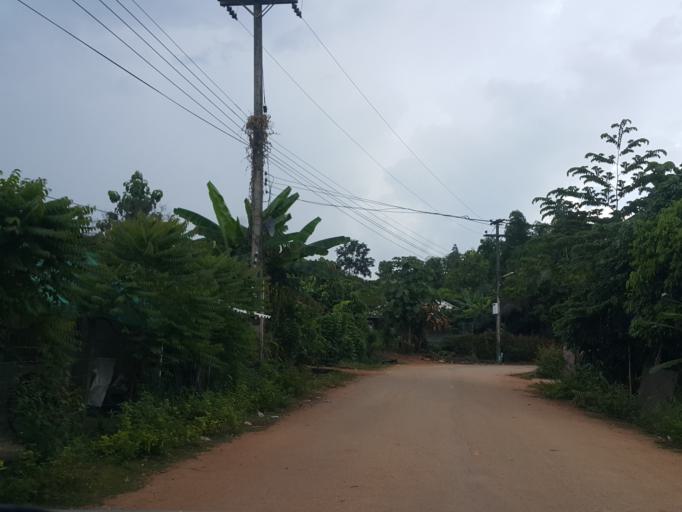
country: TH
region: Chiang Mai
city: Phrao
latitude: 19.3295
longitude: 99.1491
